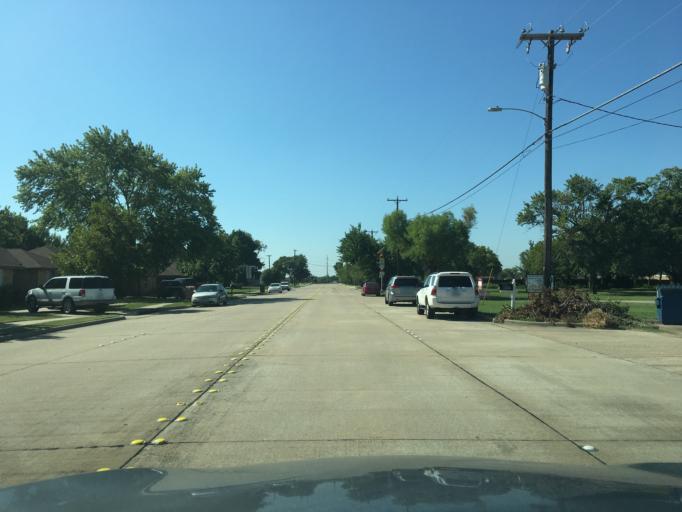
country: US
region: Texas
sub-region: Dallas County
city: Sachse
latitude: 32.9701
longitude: -96.6011
